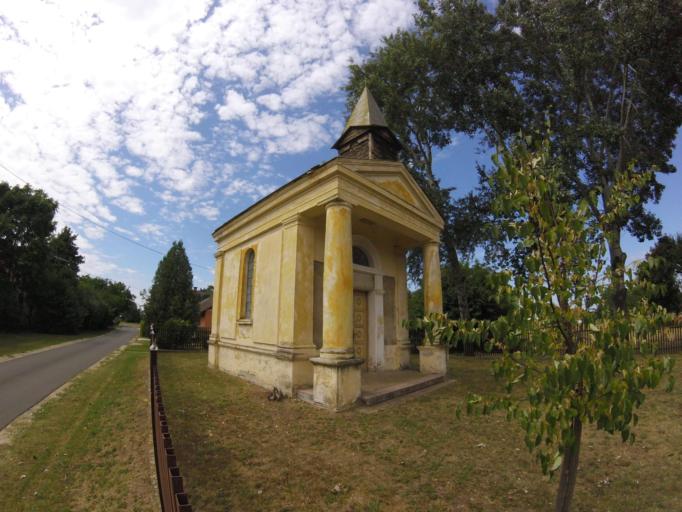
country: HU
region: Bacs-Kiskun
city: Bacsalmas
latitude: 46.0854
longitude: 19.4136
